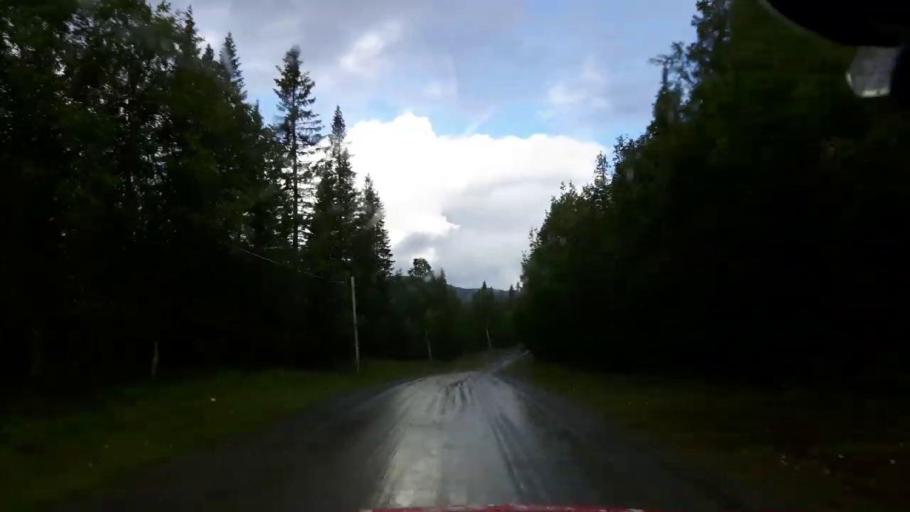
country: NO
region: Nordland
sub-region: Hattfjelldal
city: Hattfjelldal
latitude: 64.8642
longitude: 14.9071
